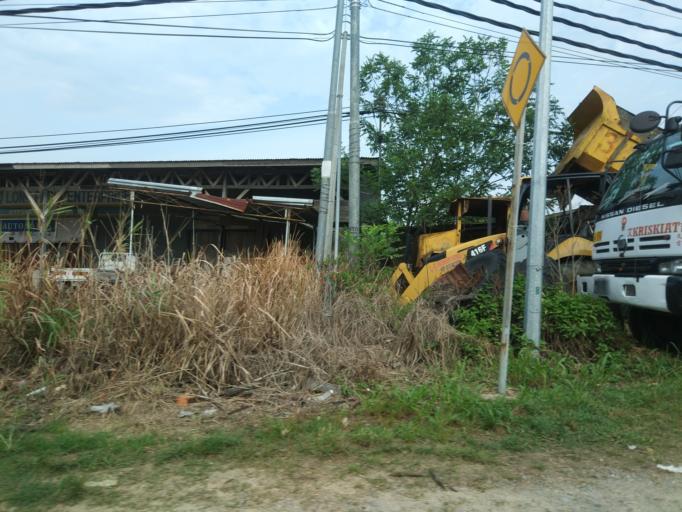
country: MY
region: Sabah
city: Beaufort
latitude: 5.0669
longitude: 115.5502
